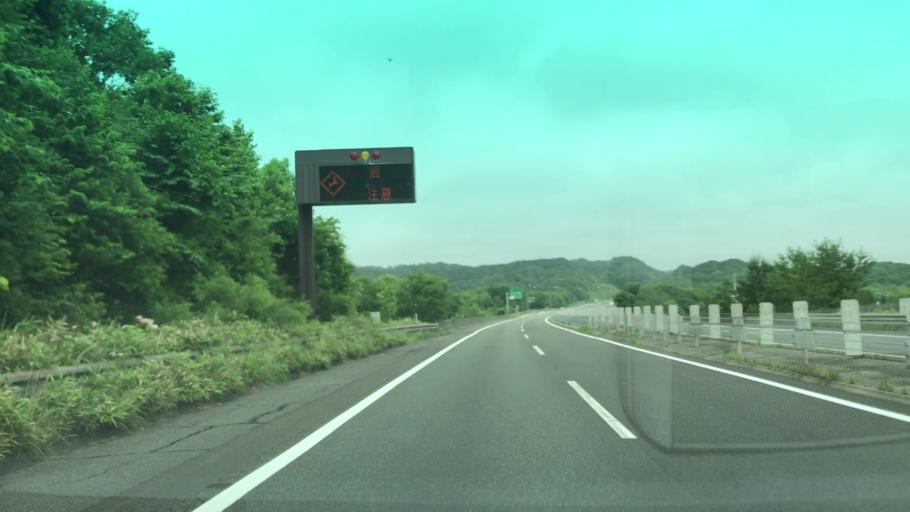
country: JP
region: Hokkaido
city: Tomakomai
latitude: 42.6289
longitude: 141.4849
